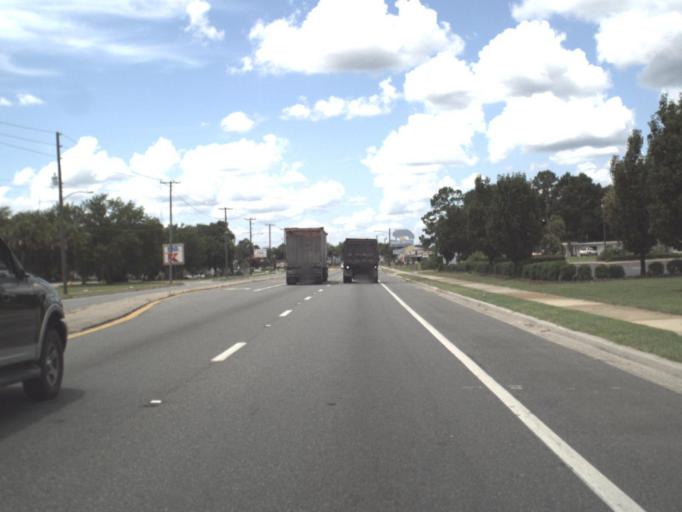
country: US
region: Florida
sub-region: Taylor County
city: Perry
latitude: 30.0995
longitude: -83.5844
